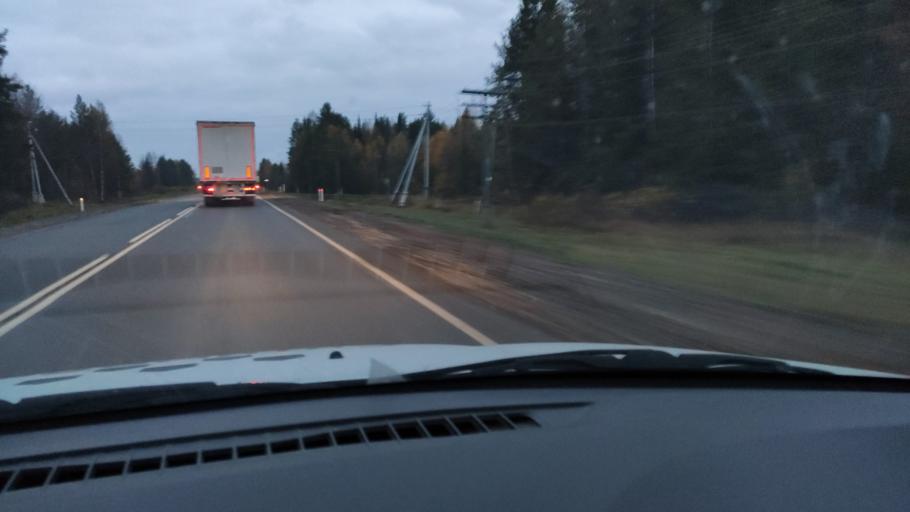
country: RU
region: Kirov
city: Kostino
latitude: 58.8388
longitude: 53.3033
